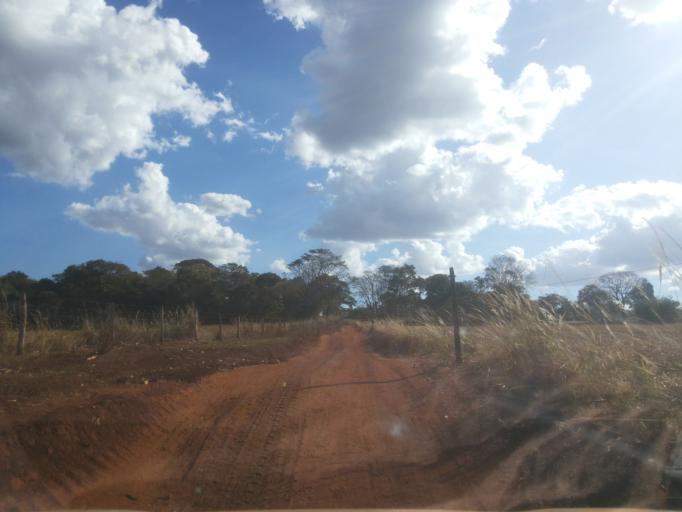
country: BR
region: Minas Gerais
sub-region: Capinopolis
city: Capinopolis
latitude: -18.6021
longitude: -49.4893
